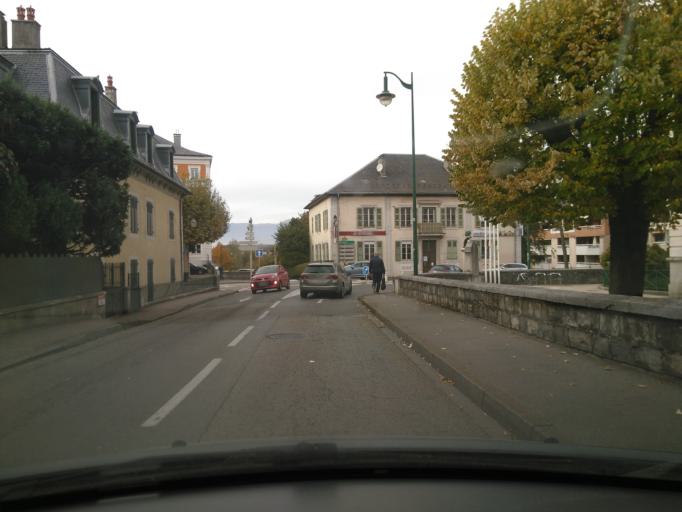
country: FR
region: Rhone-Alpes
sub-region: Departement de la Haute-Savoie
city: Saint-Julien-en-Genevois
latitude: 46.1443
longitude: 6.0823
